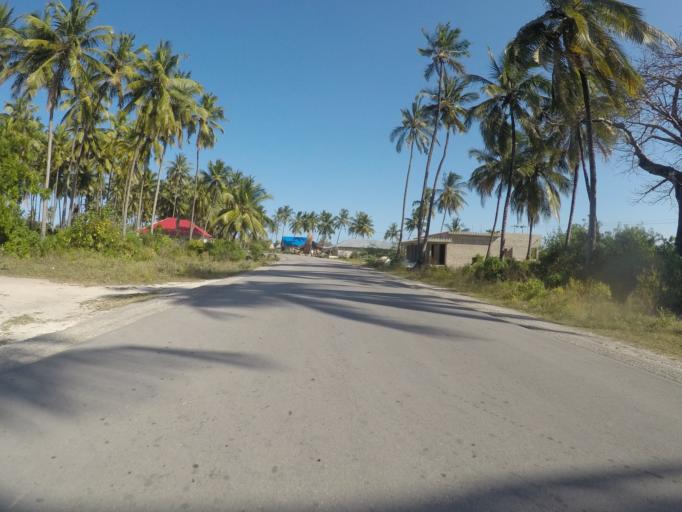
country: TZ
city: Kiwengwa
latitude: -6.1476
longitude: 39.5147
